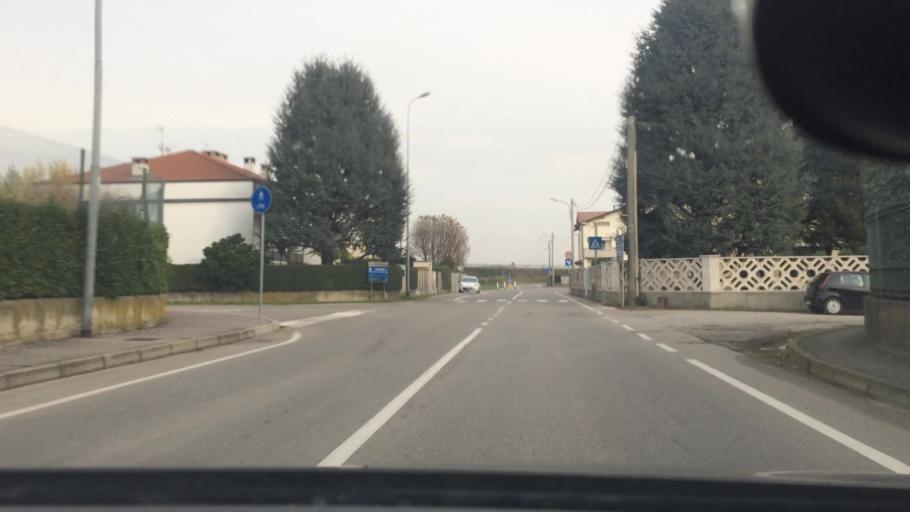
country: IT
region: Lombardy
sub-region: Provincia di Como
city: Rovellasca
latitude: 45.6648
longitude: 9.0594
